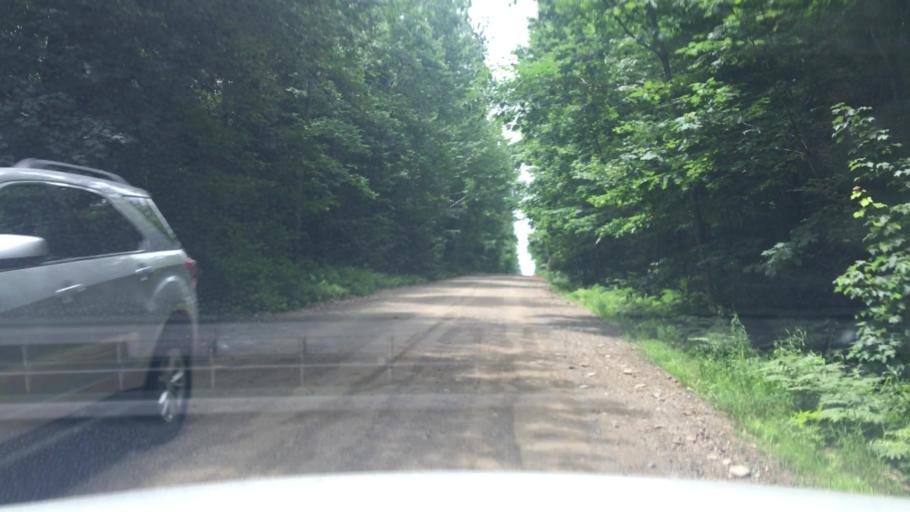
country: US
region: Maine
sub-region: Waldo County
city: Searsmont
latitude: 44.4074
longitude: -69.2718
